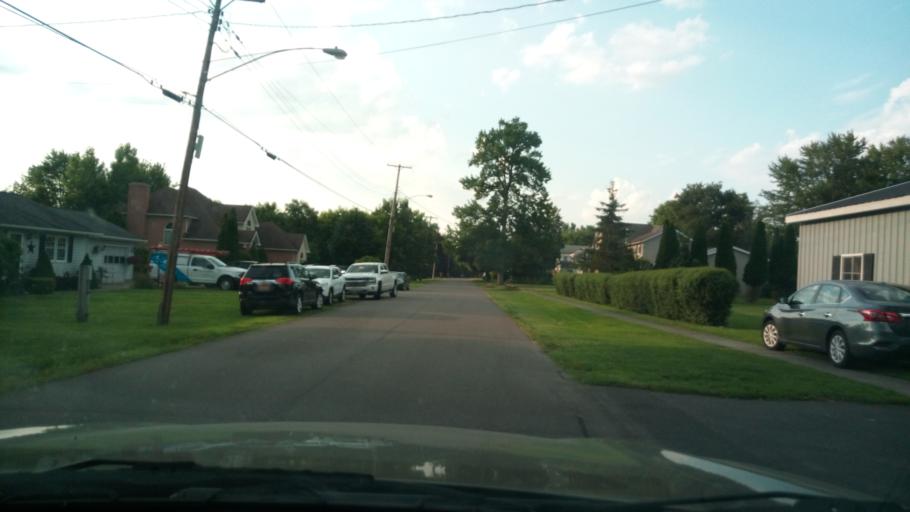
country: US
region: New York
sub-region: Wayne County
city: Clyde
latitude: 43.0890
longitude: -76.8805
